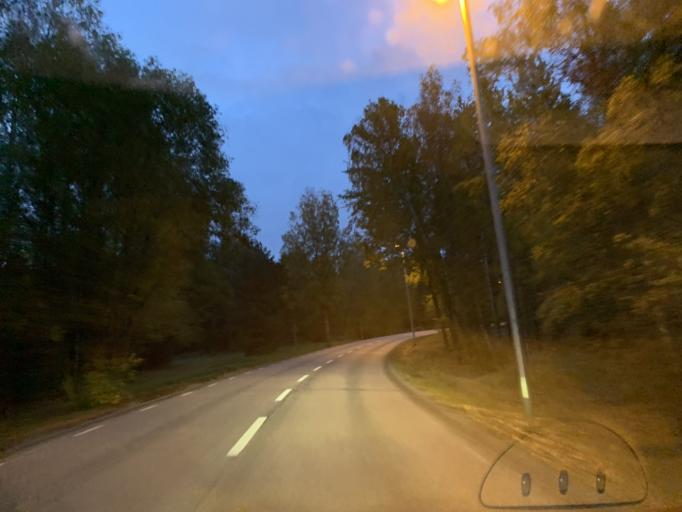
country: SE
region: Stockholm
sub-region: Botkyrka Kommun
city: Varsta
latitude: 59.1714
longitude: 17.7982
